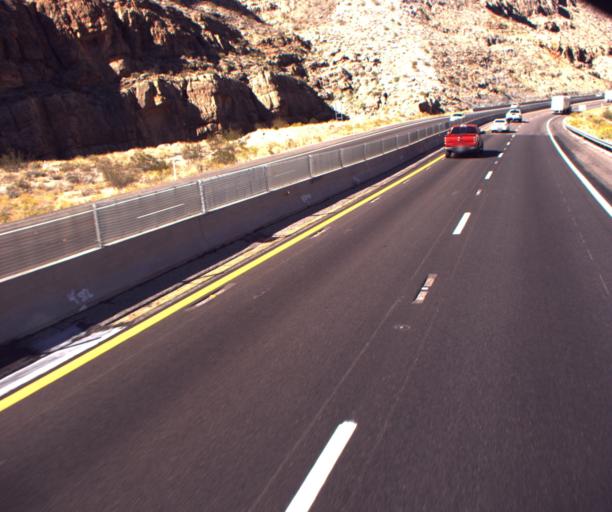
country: US
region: Arizona
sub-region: Mohave County
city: Beaver Dam
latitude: 36.9352
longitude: -113.8259
